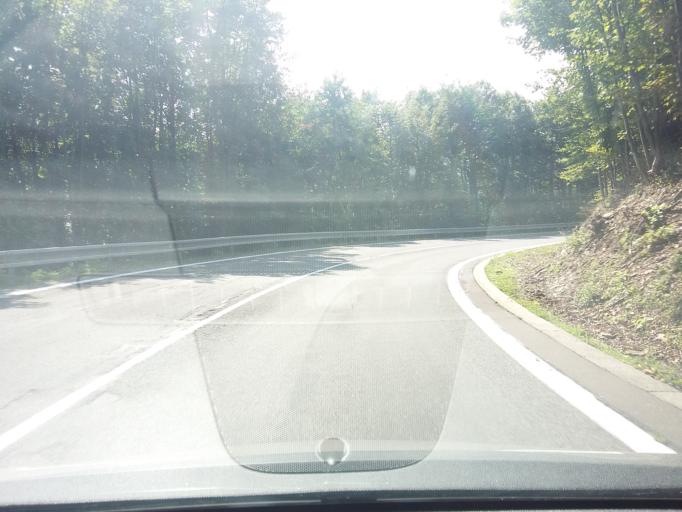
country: SK
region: Bratislavsky
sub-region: Okres Pezinok
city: Pezinok
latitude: 48.3540
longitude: 17.1943
